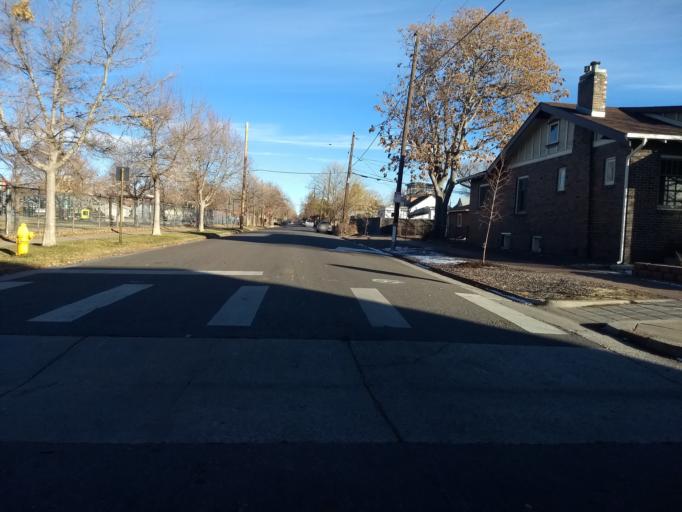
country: US
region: Colorado
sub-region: Denver County
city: Denver
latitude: 39.7194
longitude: -104.9952
